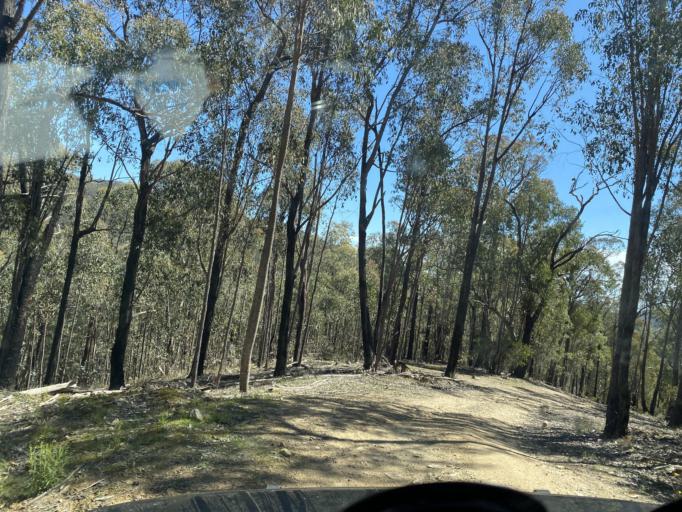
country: AU
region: Victoria
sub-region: Benalla
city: Benalla
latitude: -36.7188
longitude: 146.1808
